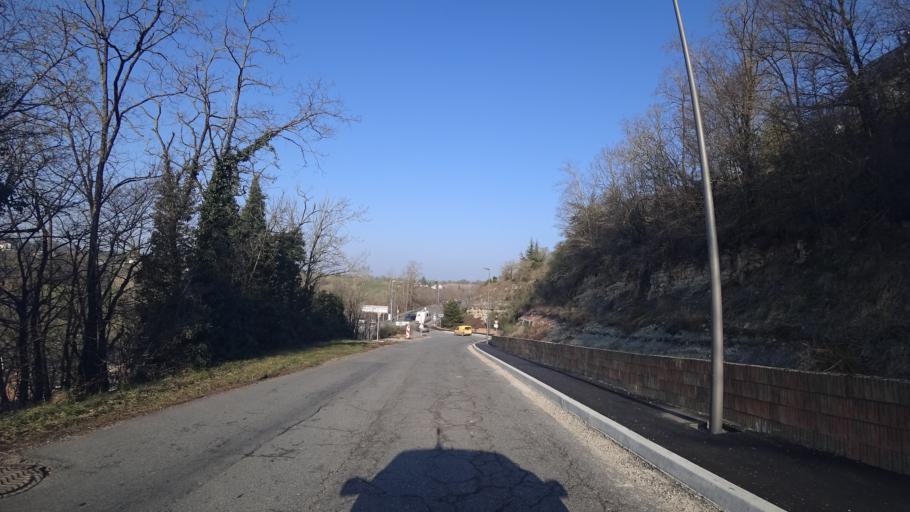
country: FR
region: Midi-Pyrenees
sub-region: Departement de l'Aveyron
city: Rodez
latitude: 44.3746
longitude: 2.5677
